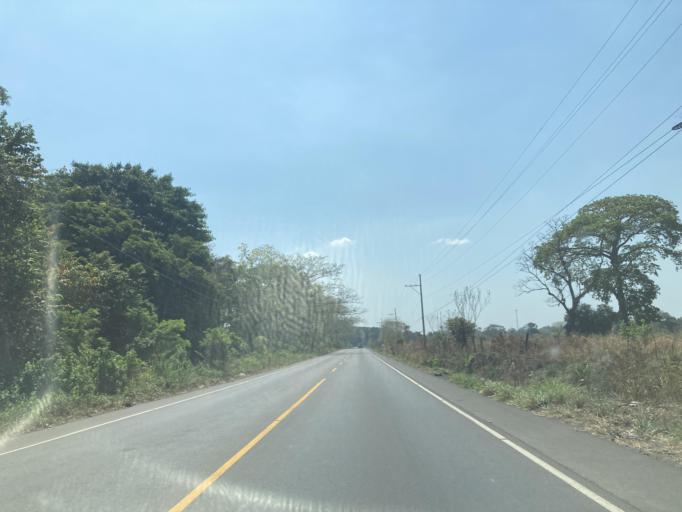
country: GT
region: Escuintla
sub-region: Municipio de Escuintla
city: Escuintla
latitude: 14.2516
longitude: -90.7421
